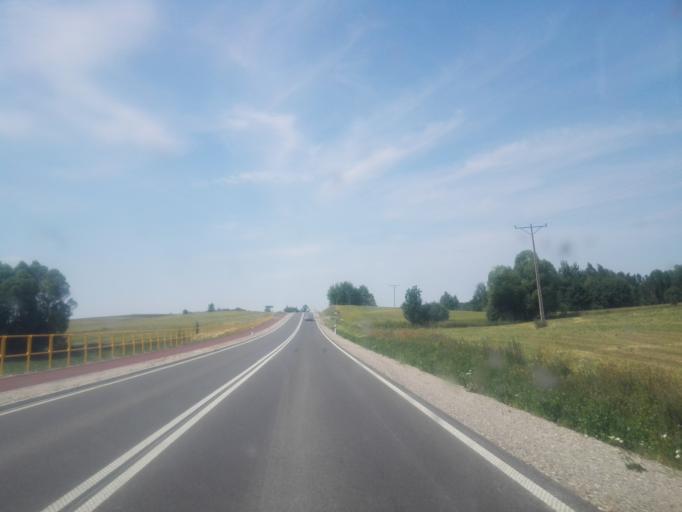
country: PL
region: Podlasie
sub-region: Powiat sejnenski
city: Sejny
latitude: 54.1090
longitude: 23.2923
